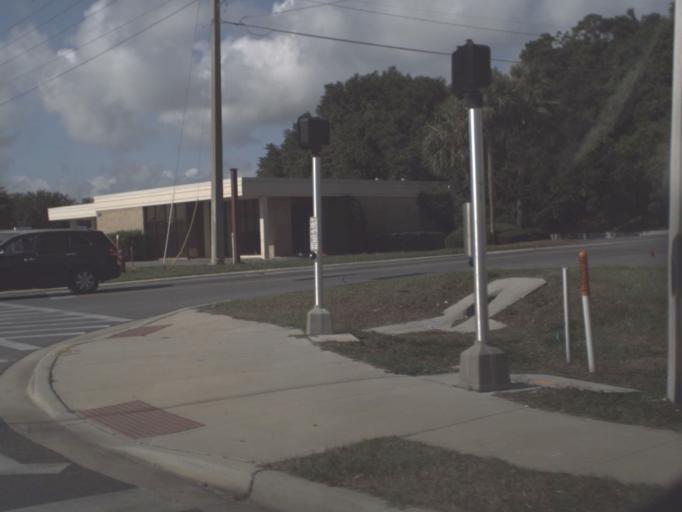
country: US
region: Florida
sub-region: Lake County
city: Fruitland Park
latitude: 28.8508
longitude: -81.9011
